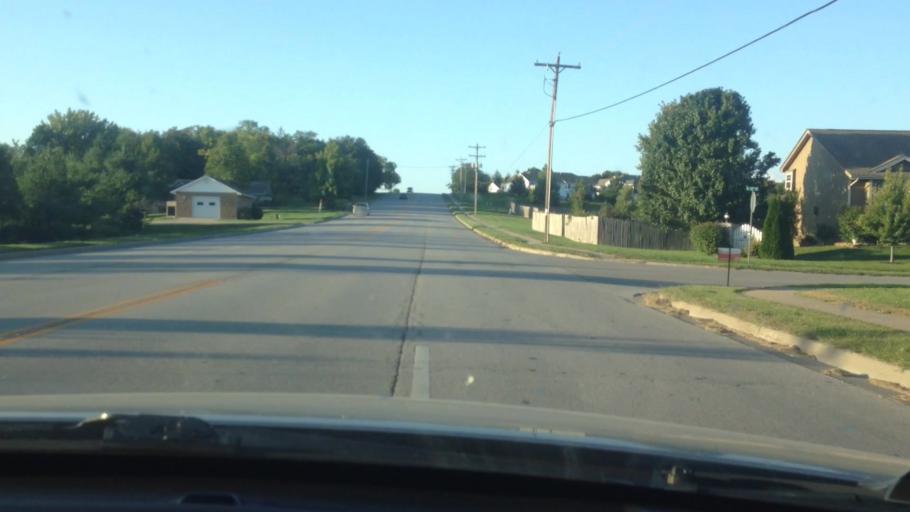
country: US
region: Missouri
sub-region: Platte County
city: Platte City
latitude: 39.3403
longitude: -94.7612
